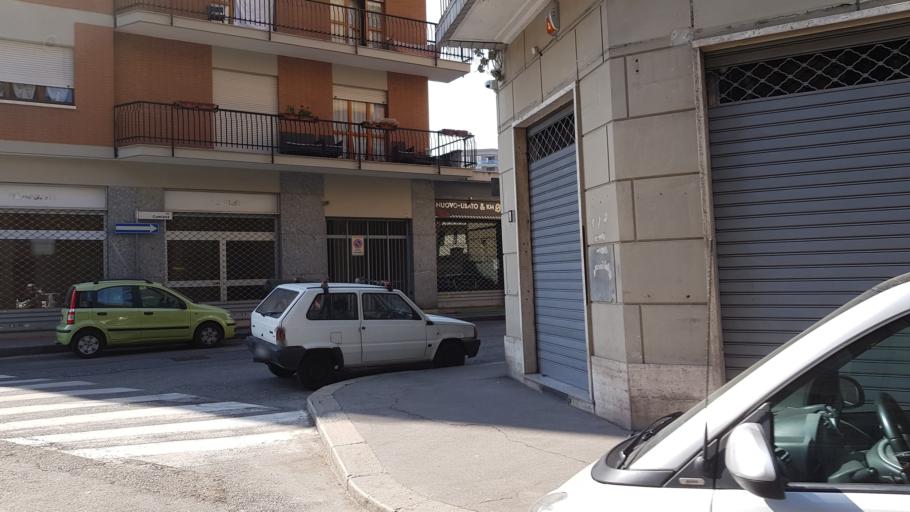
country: IT
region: Piedmont
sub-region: Provincia di Torino
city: Lesna
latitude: 45.0628
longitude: 7.6431
